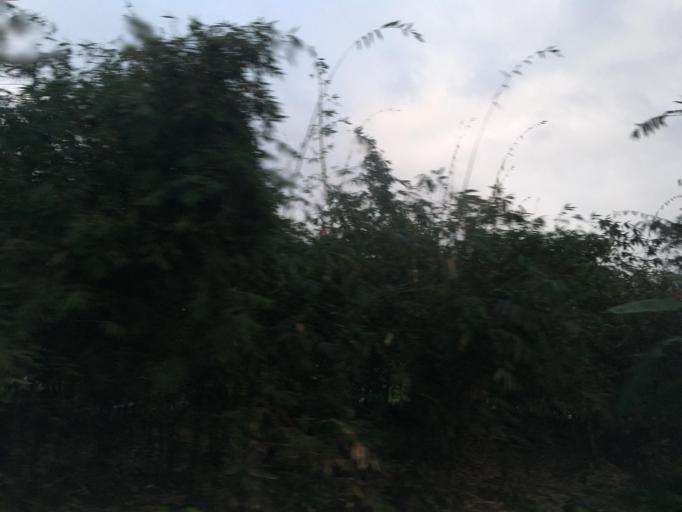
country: TW
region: Taiwan
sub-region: Yilan
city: Yilan
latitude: 24.7522
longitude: 121.7321
